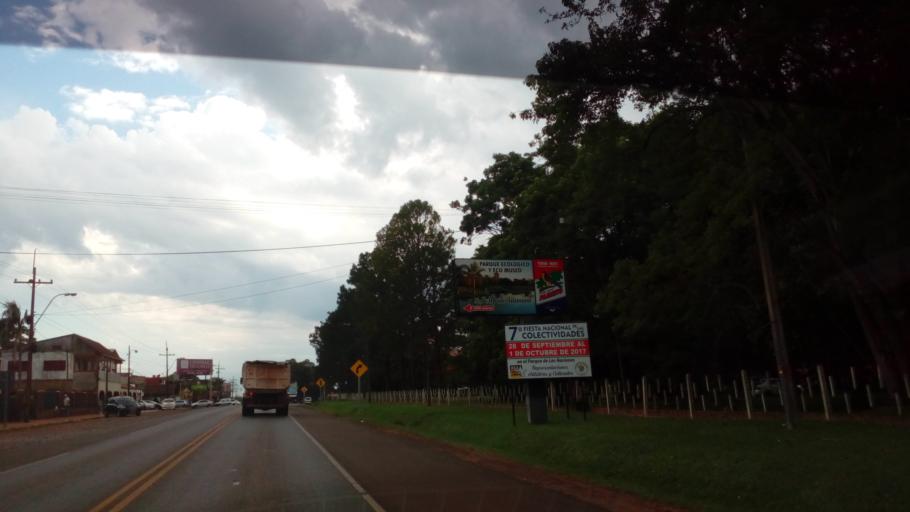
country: PY
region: Itapua
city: Obligado
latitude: -27.0743
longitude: -55.6408
